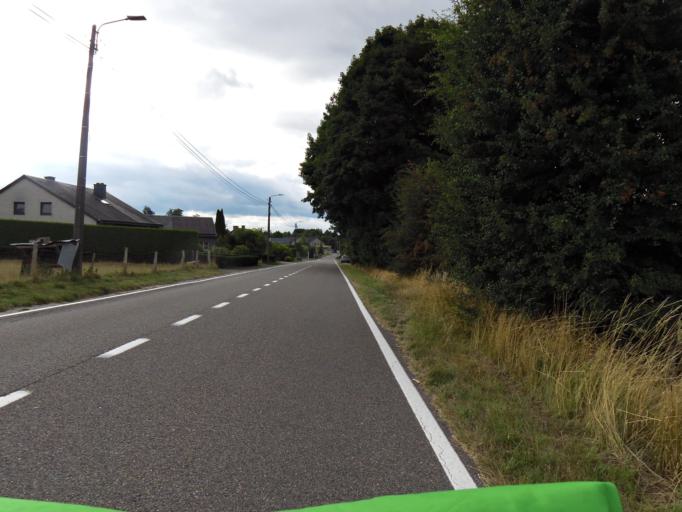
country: BE
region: Wallonia
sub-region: Province de Namur
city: Bievre
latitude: 49.9346
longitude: 5.0371
